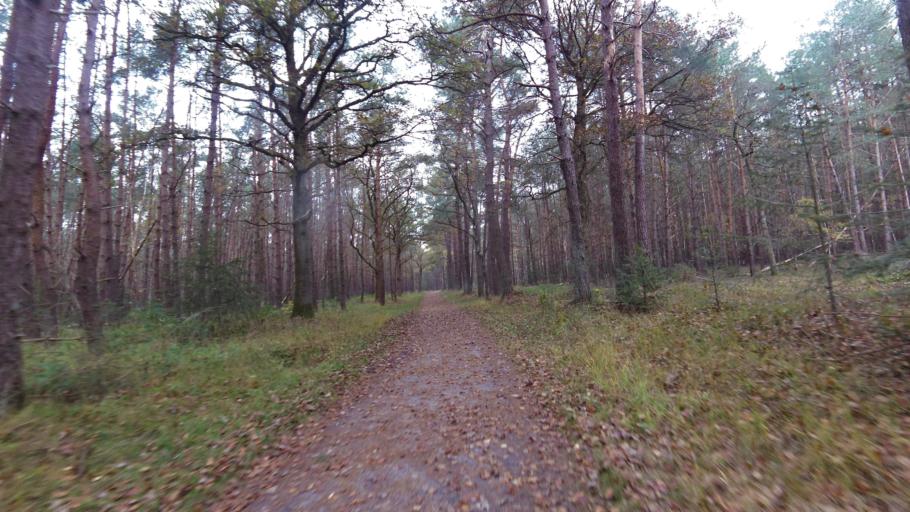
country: NL
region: North Holland
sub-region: Gemeente Hilversum
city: Hilversum
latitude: 52.1912
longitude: 5.1906
